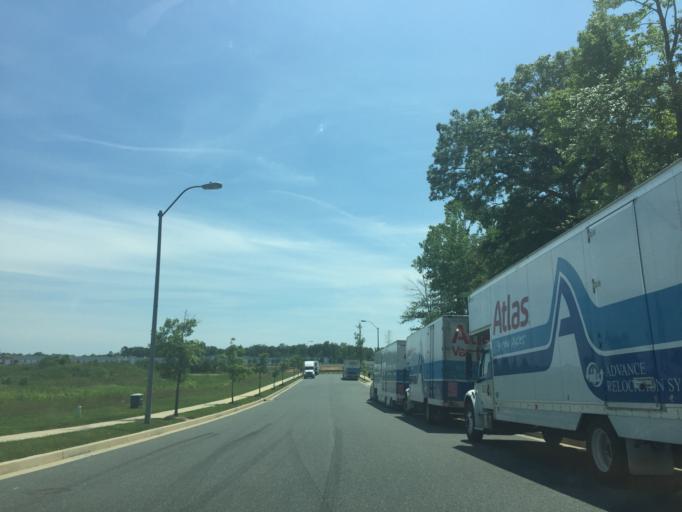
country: US
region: Maryland
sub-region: Baltimore County
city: Bowleys Quarters
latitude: 39.3519
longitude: -76.4134
